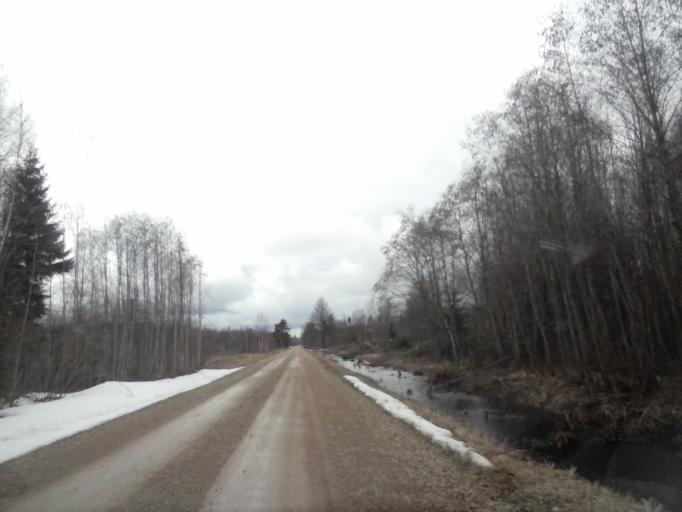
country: EE
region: Jogevamaa
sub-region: Mustvee linn
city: Mustvee
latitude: 59.0944
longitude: 26.8514
